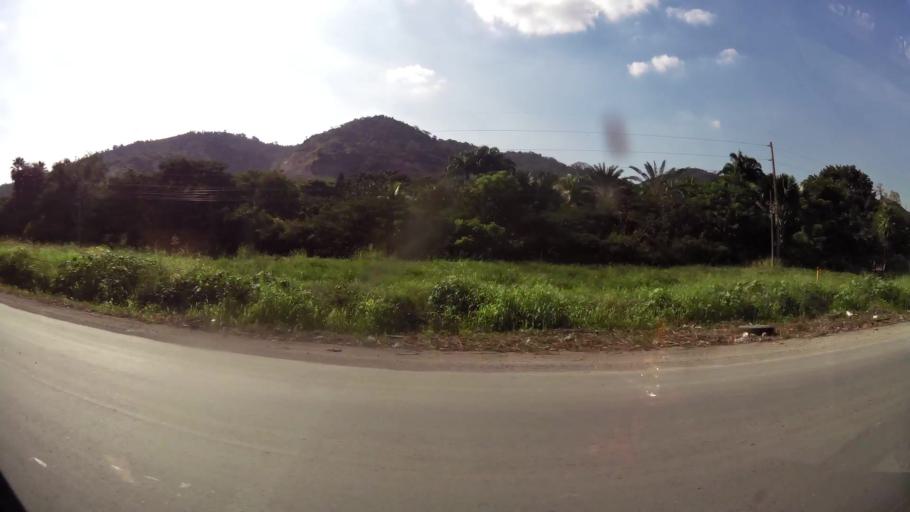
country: EC
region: Guayas
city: Santa Lucia
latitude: -2.1833
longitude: -79.9987
